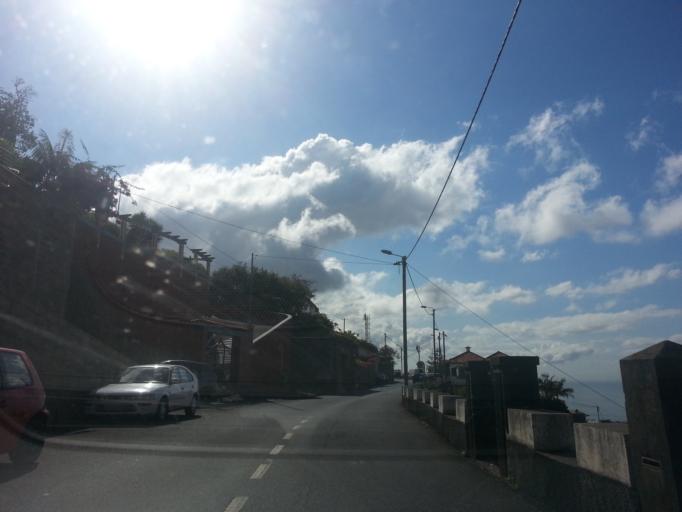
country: PT
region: Madeira
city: Camara de Lobos
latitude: 32.6709
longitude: -16.9451
